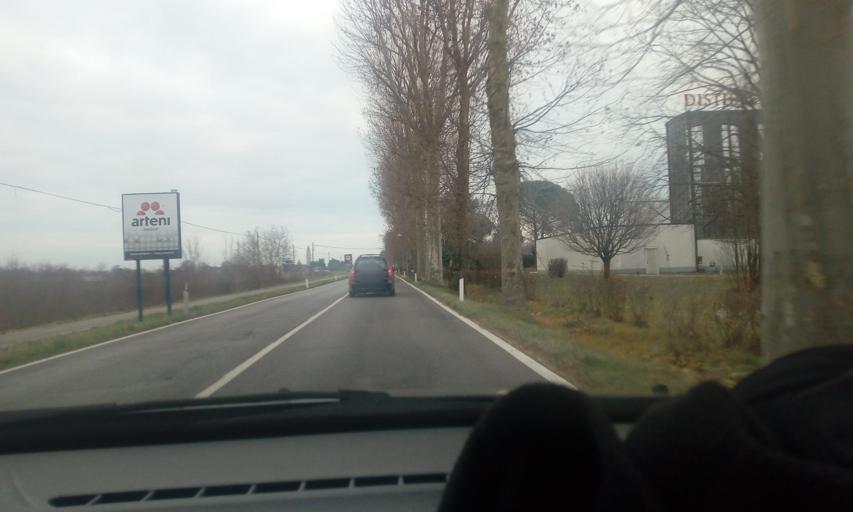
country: IT
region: Friuli Venezia Giulia
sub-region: Provincia di Udine
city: Aquileia
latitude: 45.7832
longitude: 13.3605
